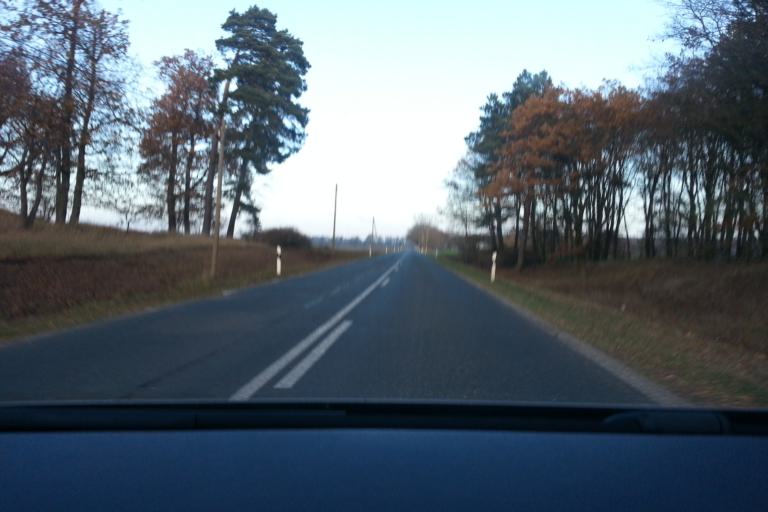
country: DE
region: Mecklenburg-Vorpommern
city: Ferdinandshof
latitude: 53.6228
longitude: 13.7921
